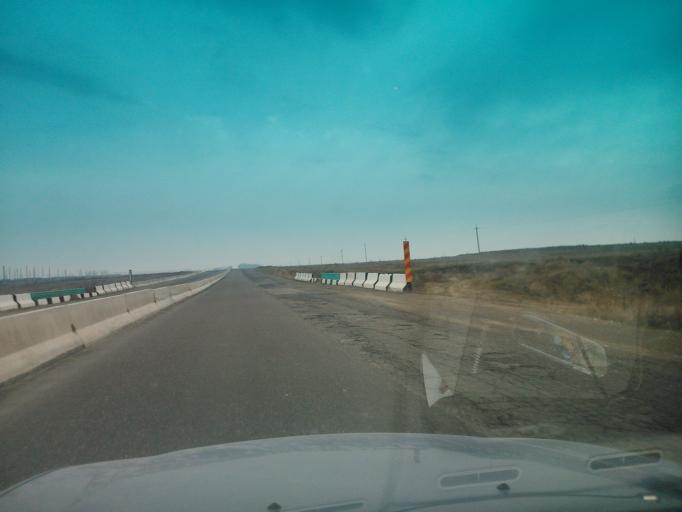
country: UZ
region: Sirdaryo
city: Yangiyer
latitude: 40.3513
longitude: 68.8054
